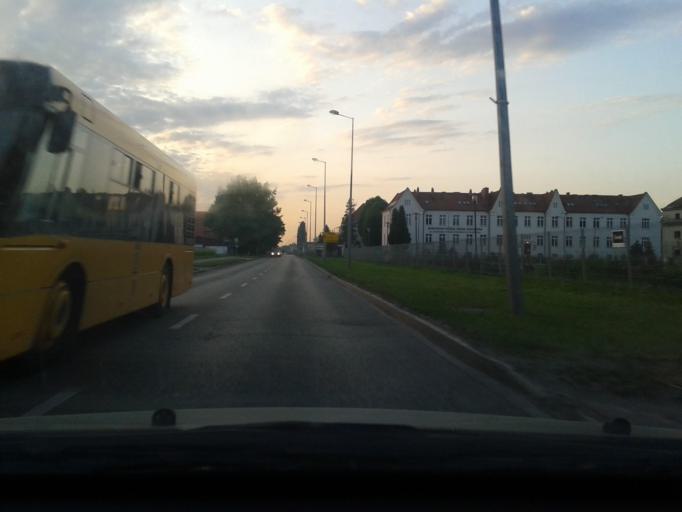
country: PL
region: Lesser Poland Voivodeship
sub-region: Powiat oswiecimski
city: Rajsko
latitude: 50.0246
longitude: 19.1985
